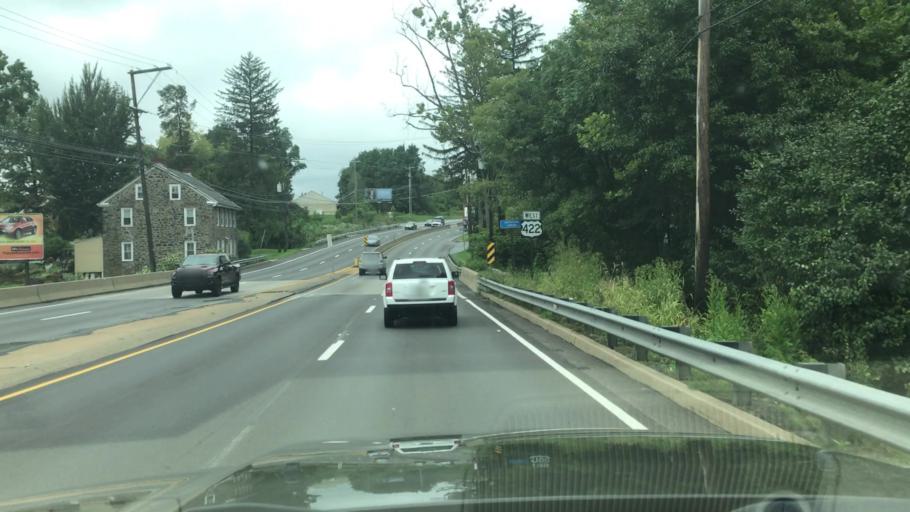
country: US
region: Pennsylvania
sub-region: Berks County
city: Lorane
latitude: 40.2993
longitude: -75.8478
